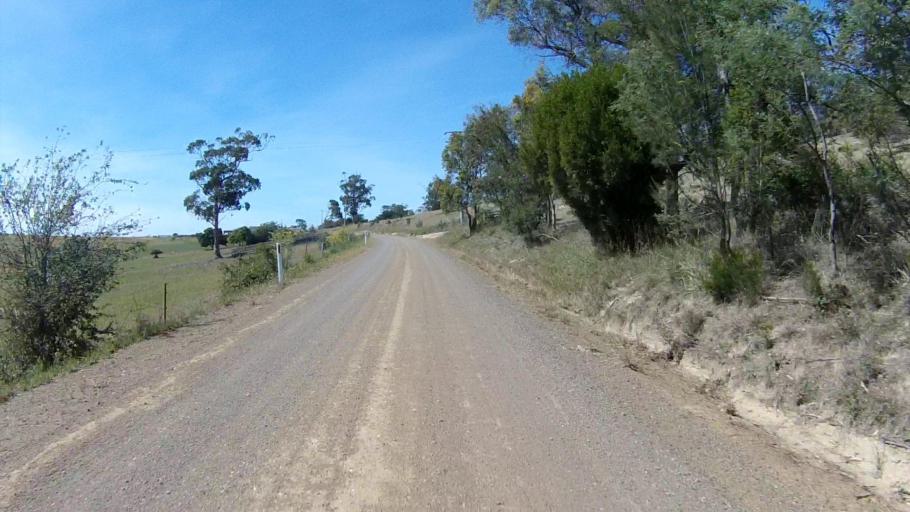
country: AU
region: Tasmania
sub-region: Sorell
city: Sorell
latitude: -42.7391
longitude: 147.5984
